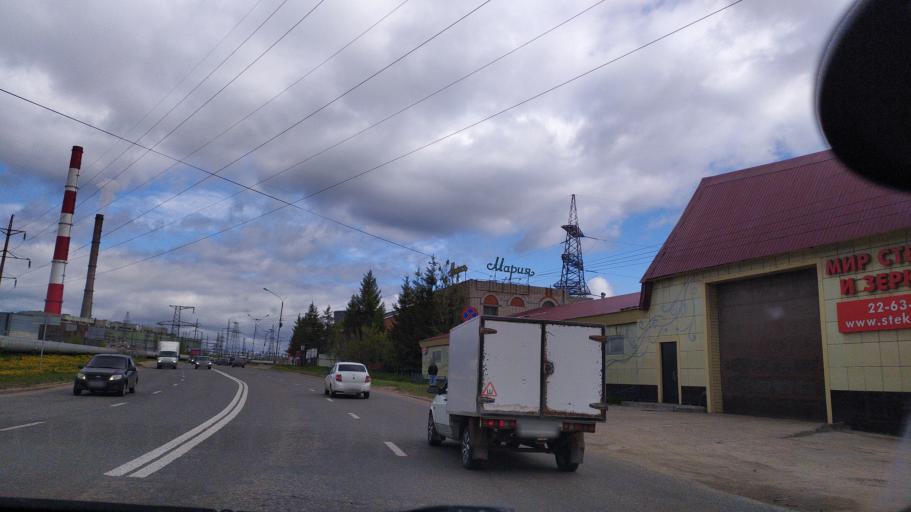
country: RU
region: Chuvashia
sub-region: Cheboksarskiy Rayon
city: Cheboksary
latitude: 56.1177
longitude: 47.3018
